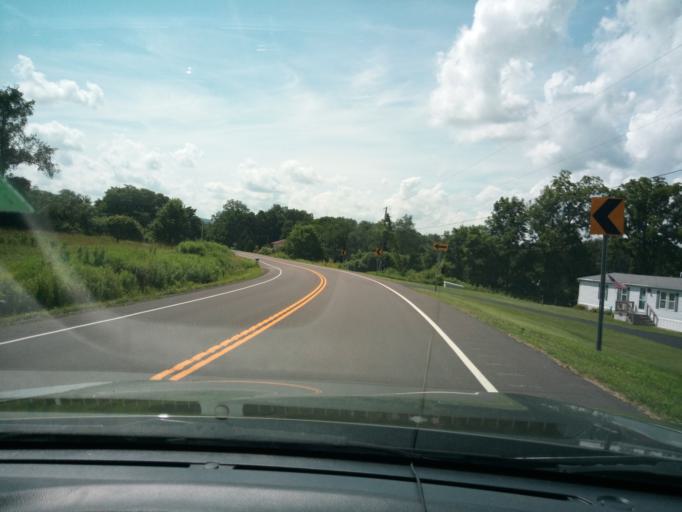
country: US
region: Pennsylvania
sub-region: Bradford County
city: South Waverly
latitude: 42.0213
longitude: -76.6746
